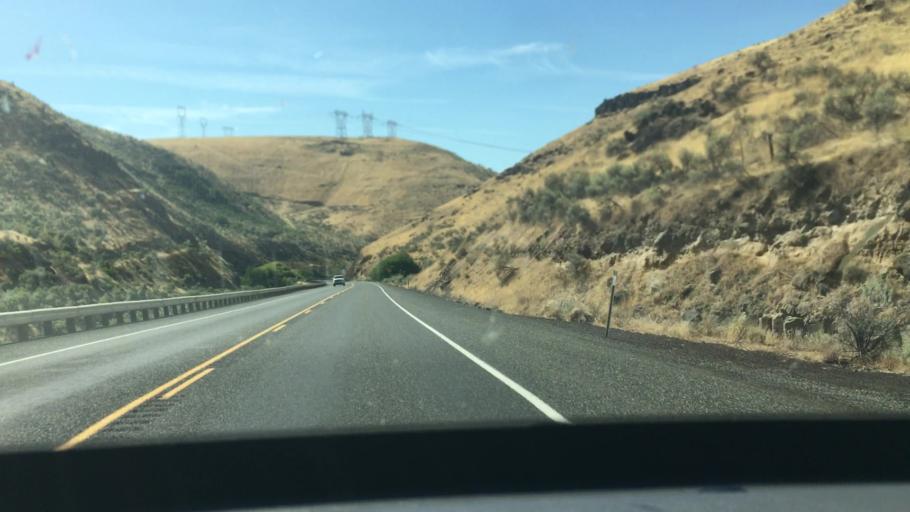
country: US
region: Washington
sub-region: Klickitat County
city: Goldendale
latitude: 45.6479
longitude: -120.8094
